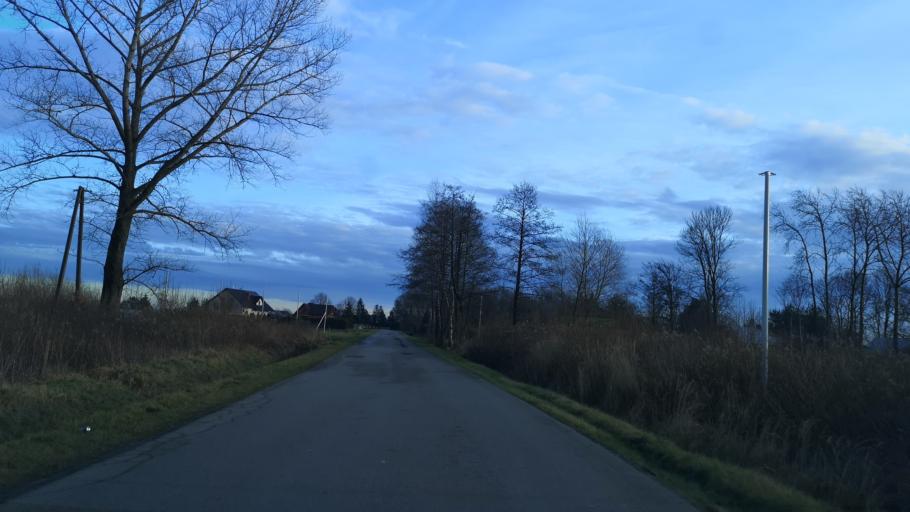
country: PL
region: Subcarpathian Voivodeship
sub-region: Powiat przeworski
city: Adamowka
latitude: 50.2450
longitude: 22.6316
